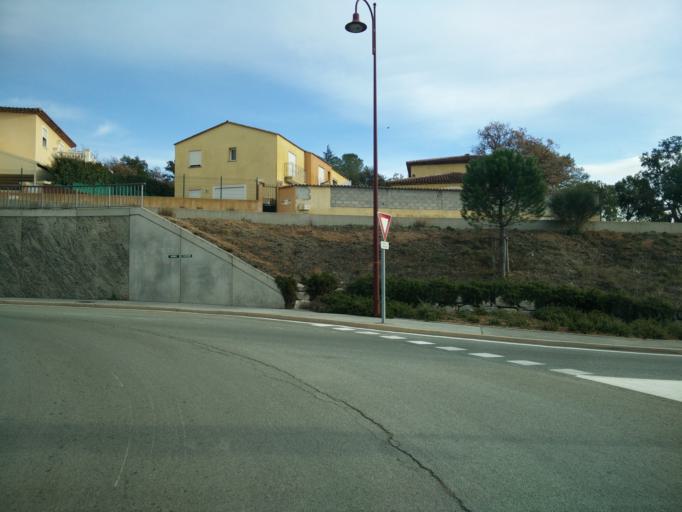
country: FR
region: Provence-Alpes-Cote d'Azur
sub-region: Departement du Var
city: Vidauban
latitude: 43.4311
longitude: 6.4366
